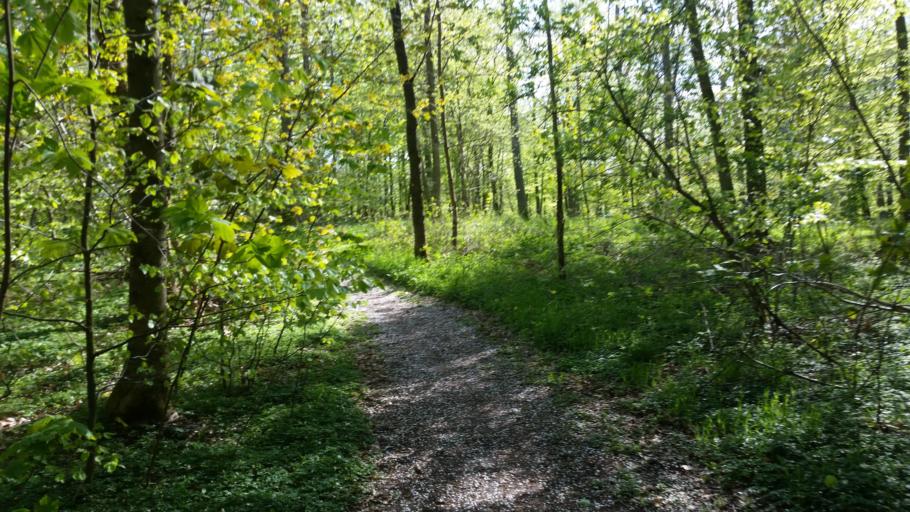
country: DK
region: Capital Region
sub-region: Helsingor Kommune
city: Hornbaek
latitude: 56.0622
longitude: 12.3727
